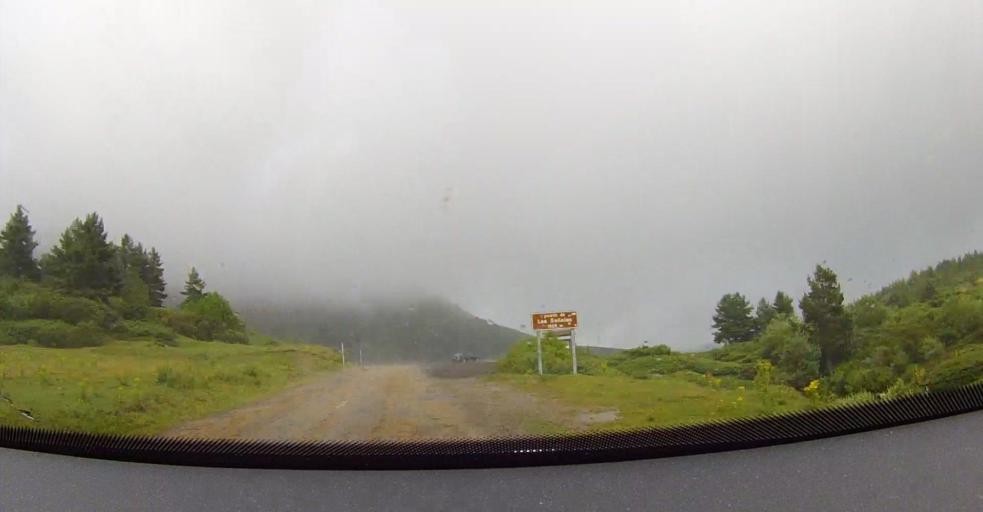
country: ES
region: Castille and Leon
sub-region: Provincia de Leon
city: Marana
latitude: 43.0757
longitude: -5.2432
